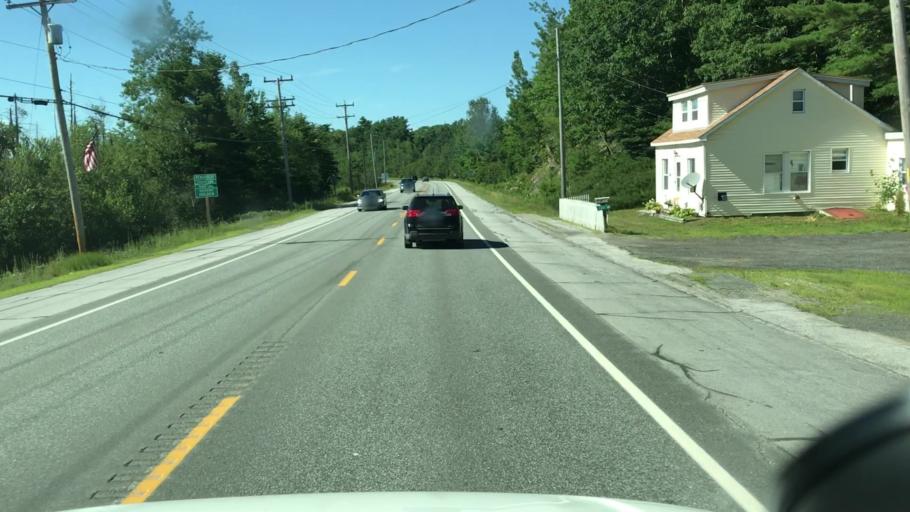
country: US
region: Maine
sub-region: Hancock County
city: Dedham
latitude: 44.7311
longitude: -68.6242
